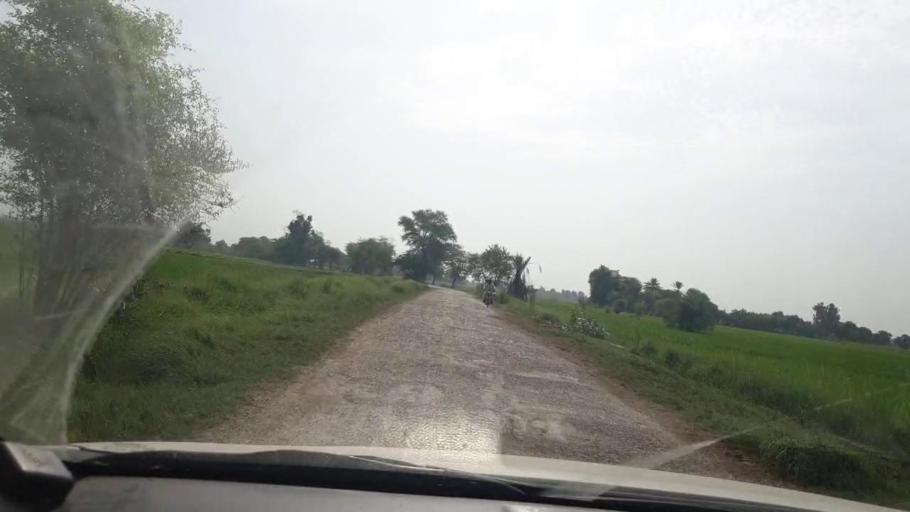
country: PK
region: Sindh
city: Lakhi
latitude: 27.8305
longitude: 68.7540
